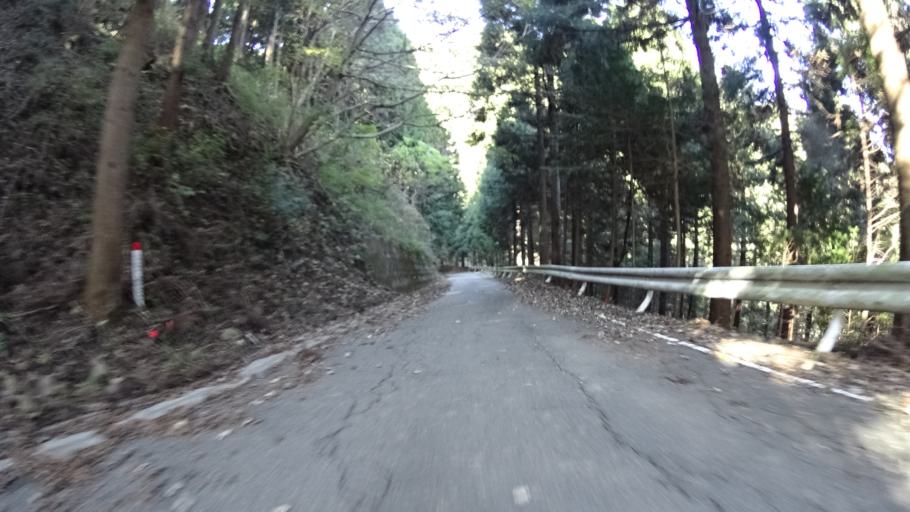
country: JP
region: Kanagawa
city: Atsugi
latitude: 35.5136
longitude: 139.2709
